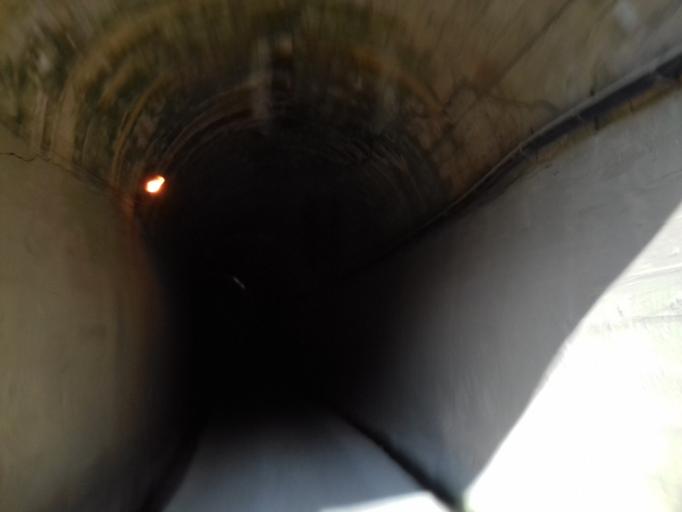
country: CO
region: Tolima
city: Ibague
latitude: 4.4159
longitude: -75.2741
